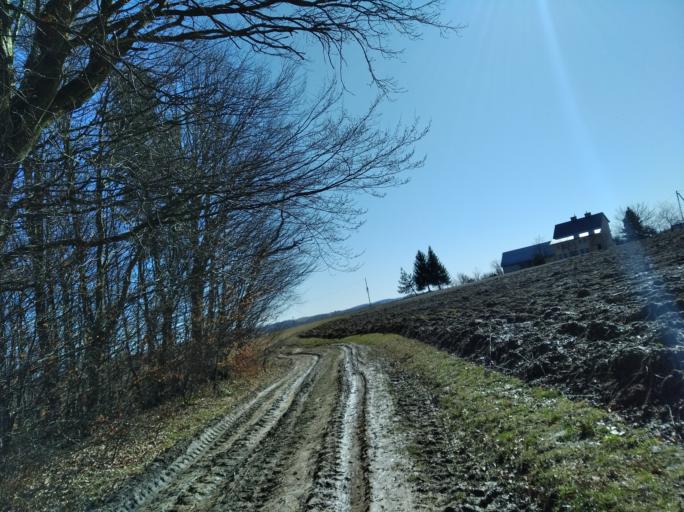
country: PL
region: Subcarpathian Voivodeship
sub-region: Powiat strzyzowski
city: Wisniowa
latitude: 49.9243
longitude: 21.6718
